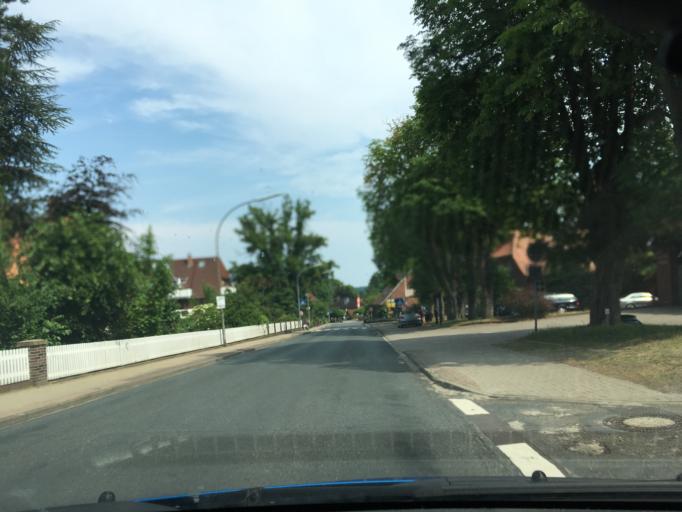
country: DE
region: Lower Saxony
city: Hanstedt
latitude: 53.2588
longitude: 10.0099
